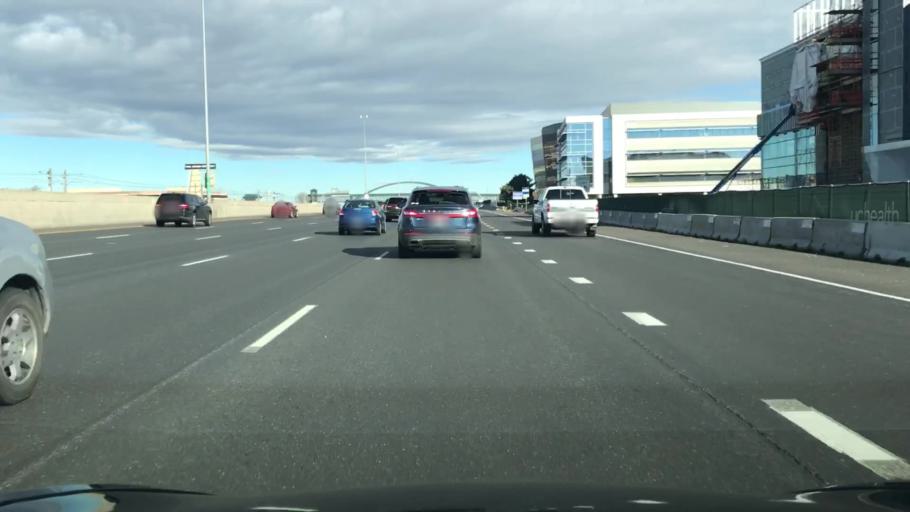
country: US
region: Colorado
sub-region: Arapahoe County
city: Centennial
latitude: 39.5730
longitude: -104.8725
